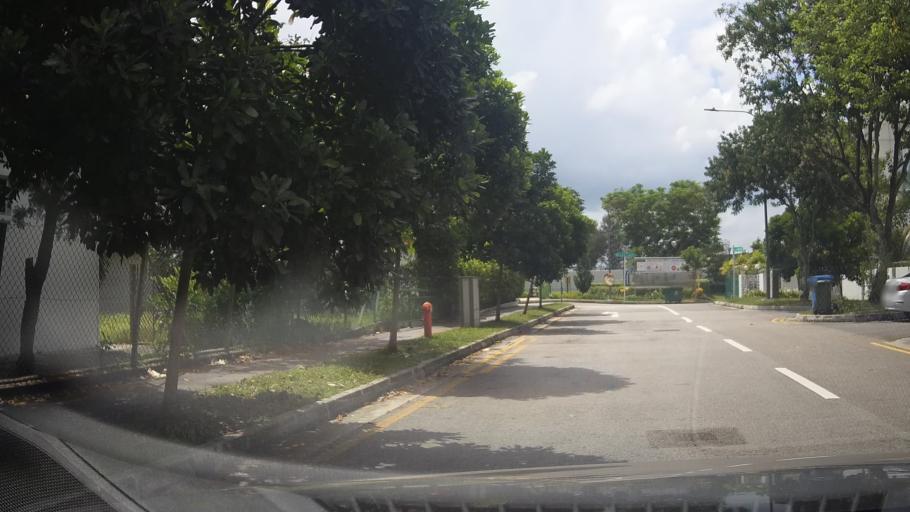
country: SG
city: Singapore
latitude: 1.3118
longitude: 103.8921
